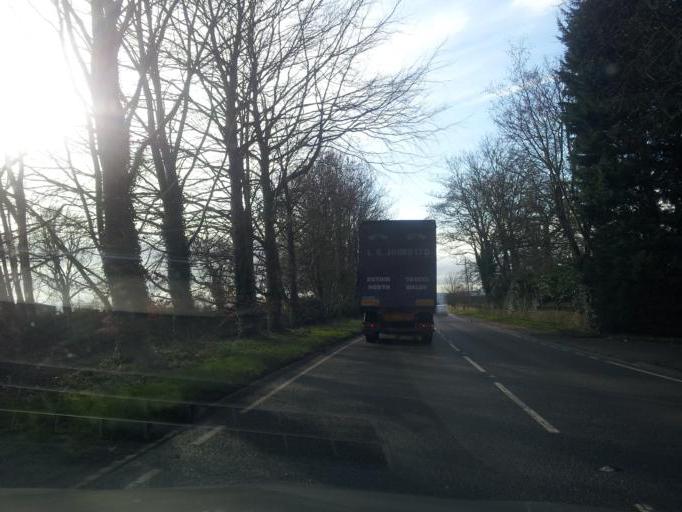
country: GB
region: England
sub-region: District of Rutland
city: Ketton
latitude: 52.6107
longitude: -0.5324
